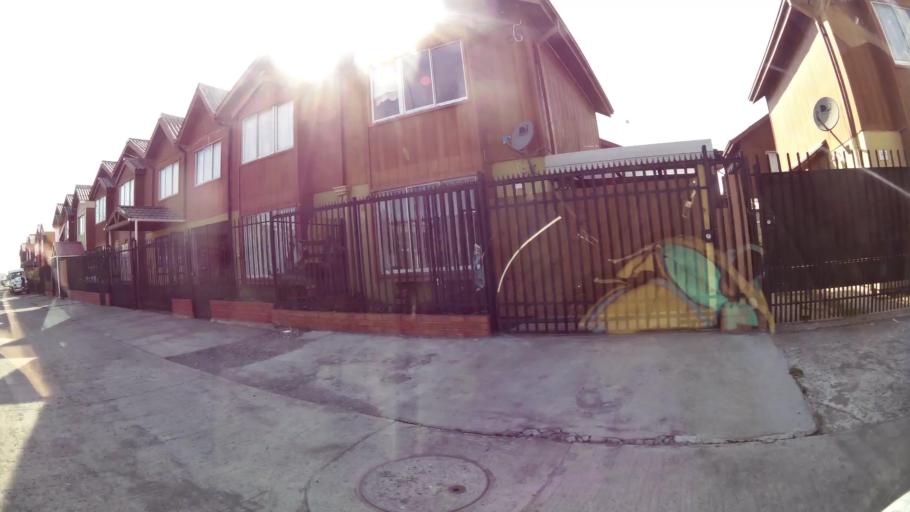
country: CL
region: Biobio
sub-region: Provincia de Concepcion
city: Talcahuano
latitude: -36.7928
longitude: -73.1151
